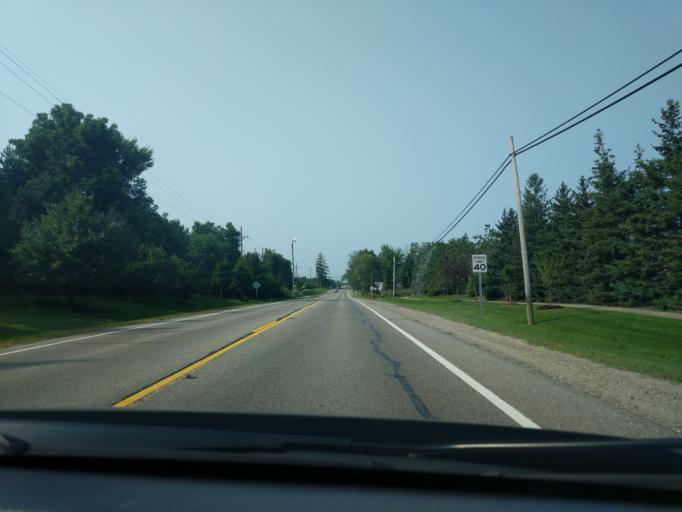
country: US
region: Michigan
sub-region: Oakland County
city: Walled Lake
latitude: 42.5139
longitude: -83.5019
